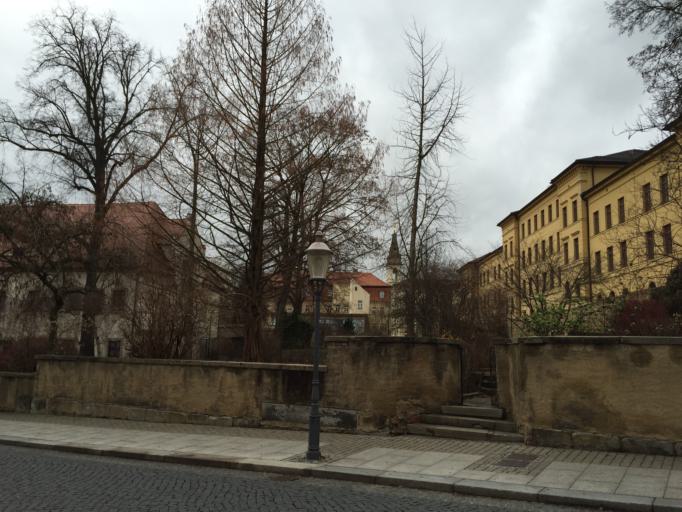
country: DE
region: Saxony
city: Zittau
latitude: 50.8982
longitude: 14.8092
